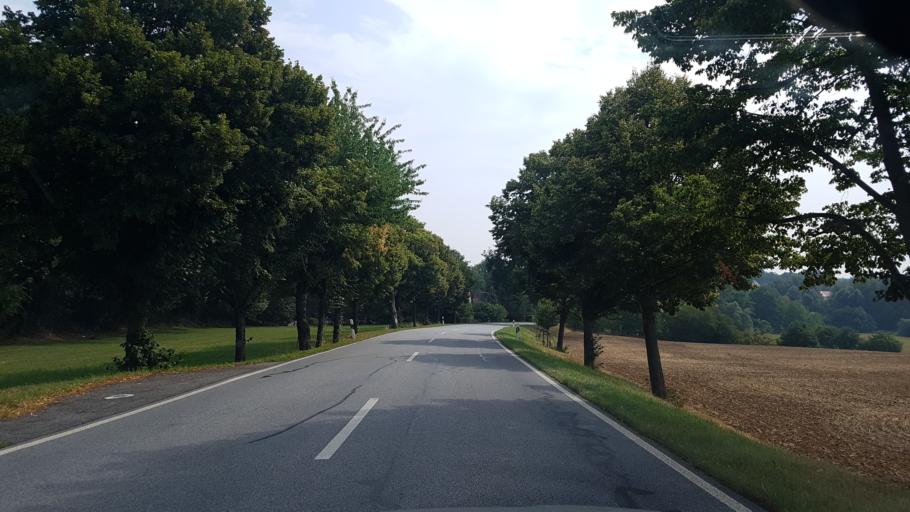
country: DE
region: Saxony
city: Goda
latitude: 51.2072
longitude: 14.2987
